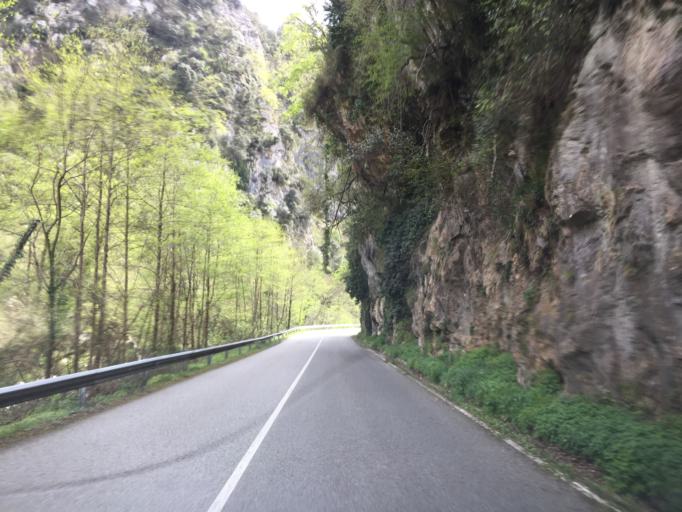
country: ES
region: Asturias
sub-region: Province of Asturias
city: Proaza
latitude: 43.2362
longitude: -6.0312
